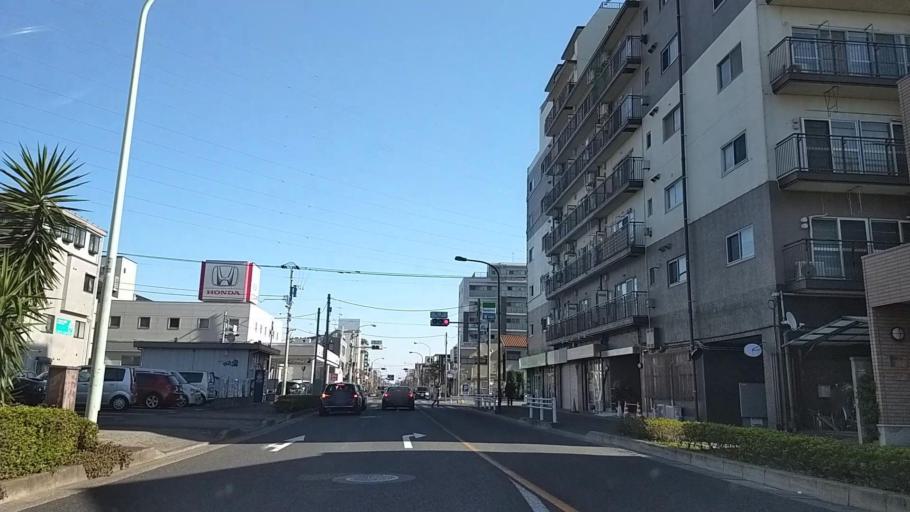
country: JP
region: Tokyo
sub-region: Machida-shi
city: Machida
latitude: 35.5518
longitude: 139.4395
